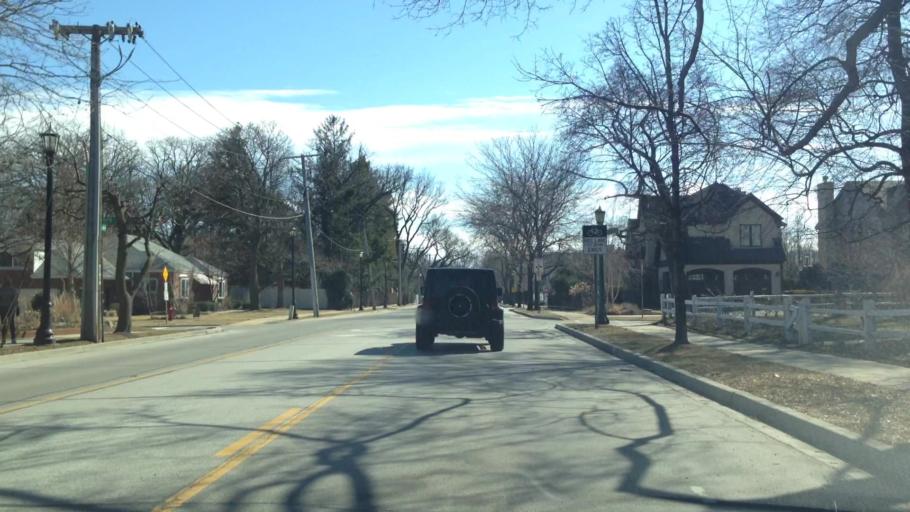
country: US
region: Illinois
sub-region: Cook County
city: Evanston
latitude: 42.0716
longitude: -87.6828
